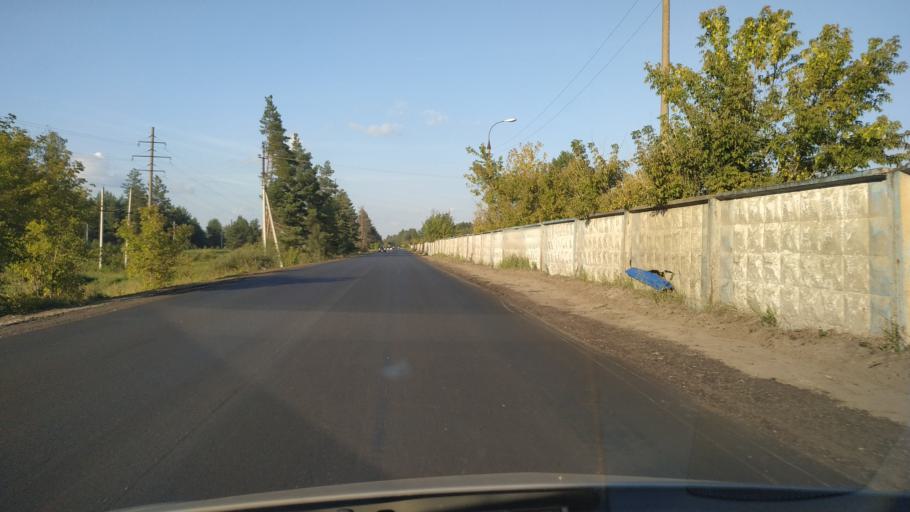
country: RU
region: Moskovskaya
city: Kerva
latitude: 55.5755
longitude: 39.6822
